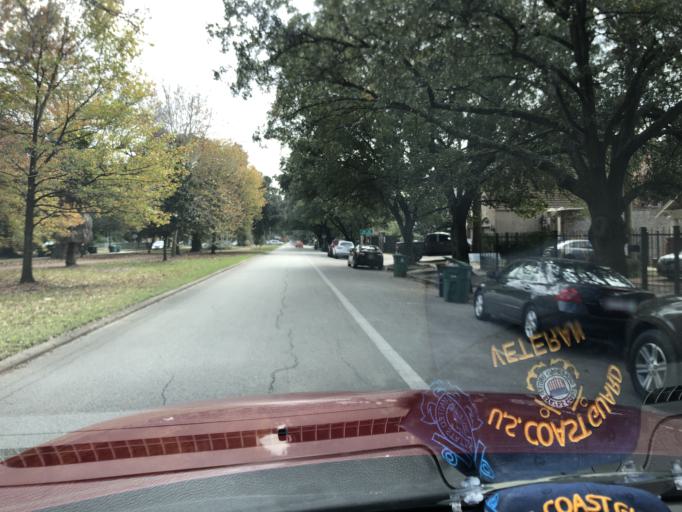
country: US
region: Texas
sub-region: Harris County
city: Houston
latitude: 29.7925
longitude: -95.3979
